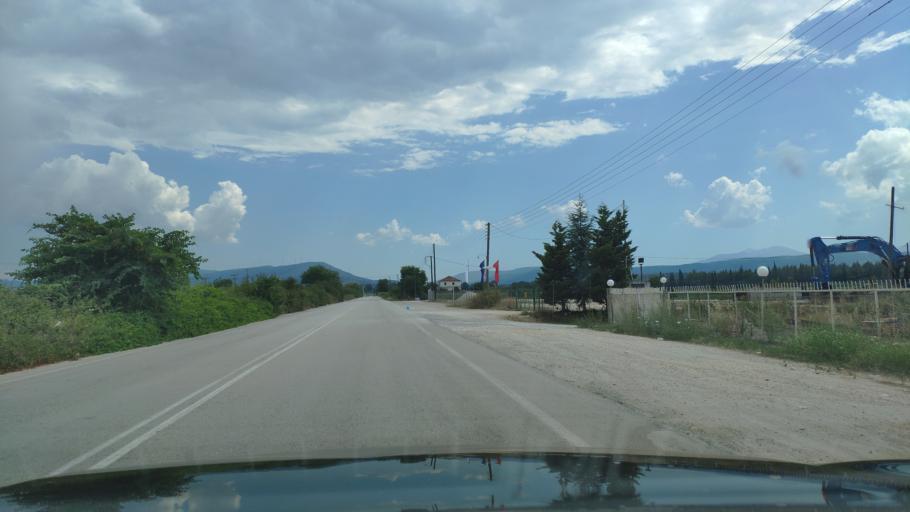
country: GR
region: West Greece
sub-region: Nomos Aitolias kai Akarnanias
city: Krikellos
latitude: 38.9381
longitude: 21.1769
